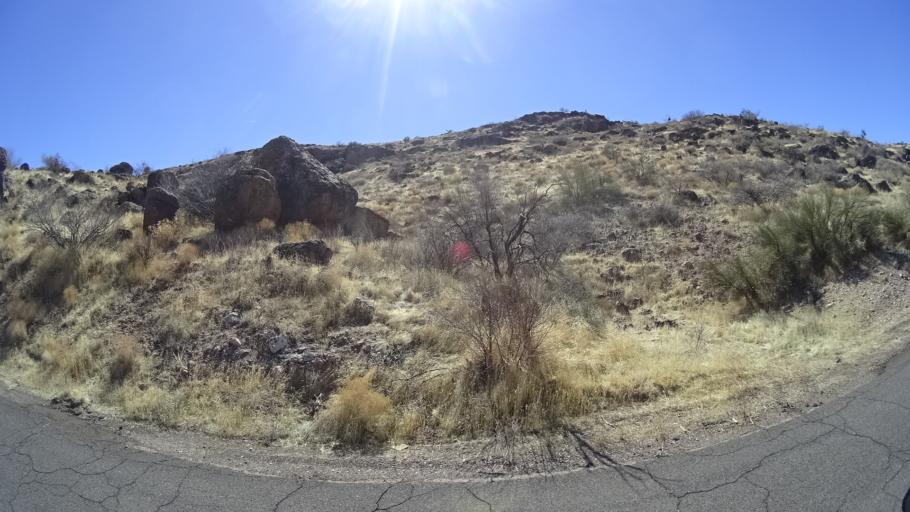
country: US
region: Arizona
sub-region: Mohave County
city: Kingman
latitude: 35.1815
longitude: -114.0588
